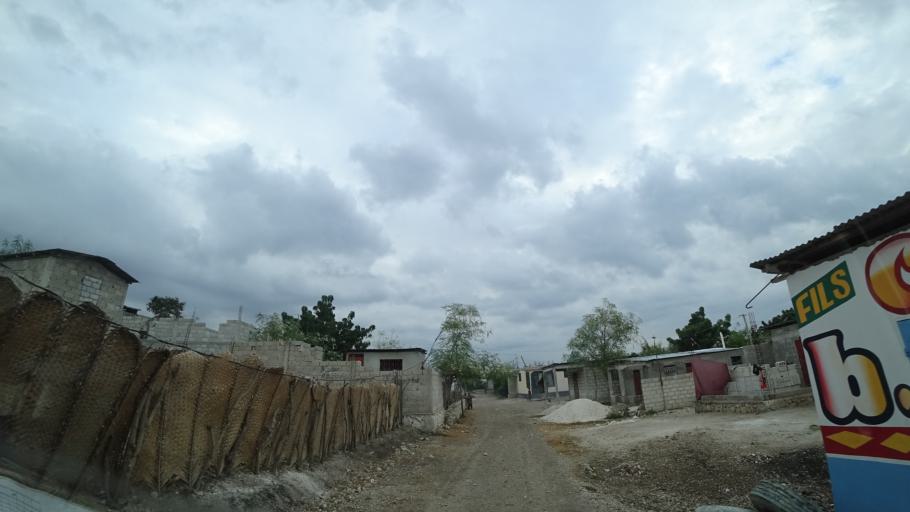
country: HT
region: Ouest
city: Croix des Bouquets
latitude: 18.6495
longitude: -72.2792
